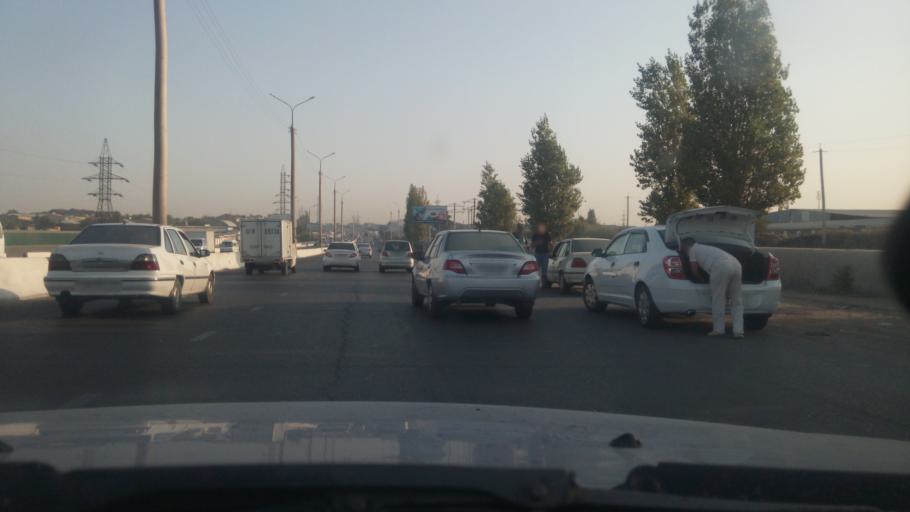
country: UZ
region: Toshkent Shahri
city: Tashkent
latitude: 41.2788
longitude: 69.1470
